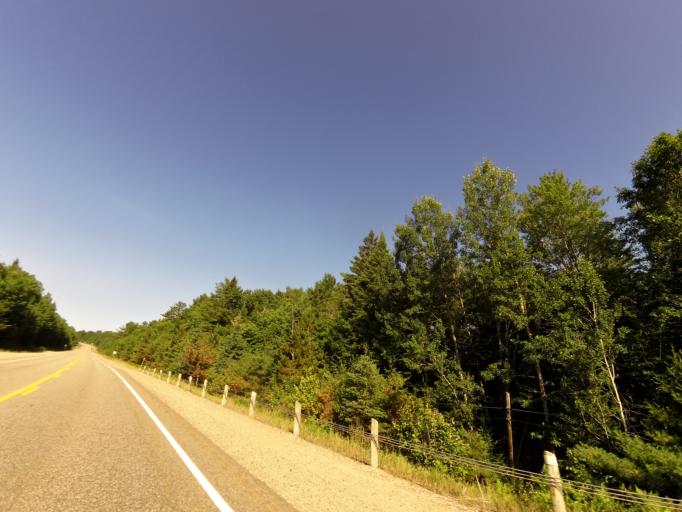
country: CA
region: Ontario
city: Deep River
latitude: 46.1801
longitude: -77.6755
